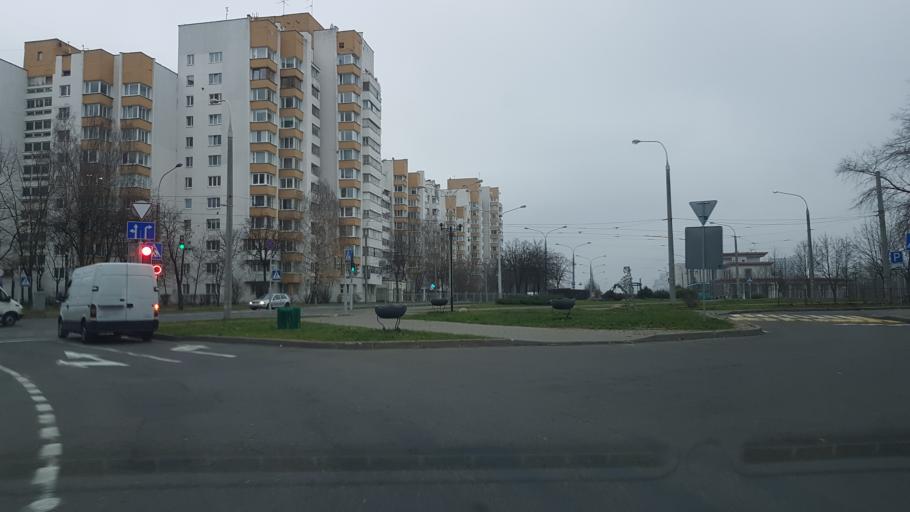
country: BY
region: Minsk
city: Minsk
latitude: 53.9264
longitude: 27.5444
